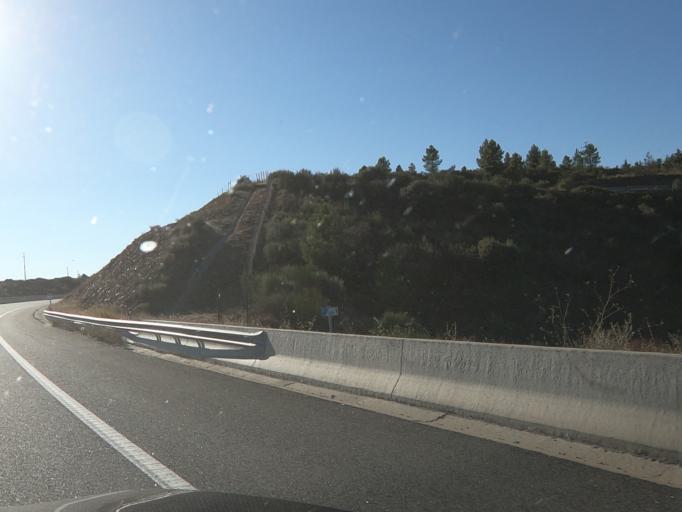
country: PT
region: Vila Real
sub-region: Murca
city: Murca
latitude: 41.4212
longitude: -7.3720
